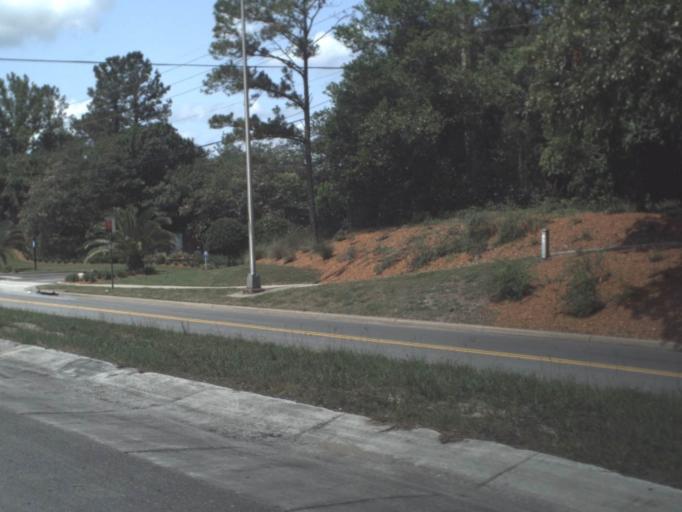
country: US
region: Florida
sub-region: Duval County
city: Jacksonville
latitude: 30.2355
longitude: -81.5522
